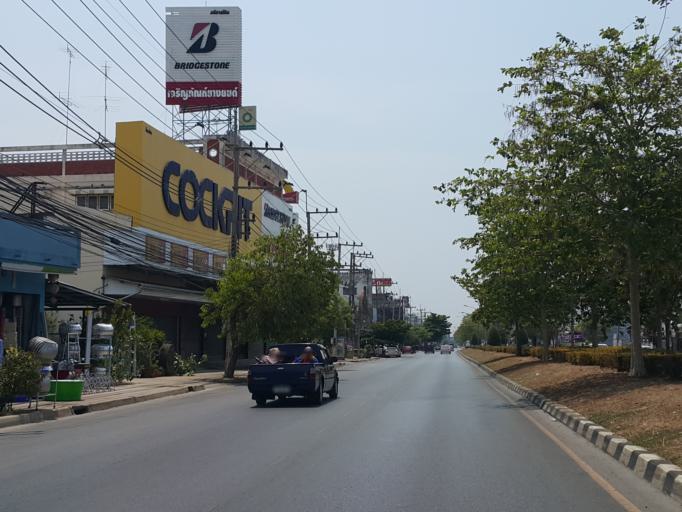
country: TH
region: Kanchanaburi
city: Kanchanaburi
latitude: 14.0382
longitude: 99.5189
